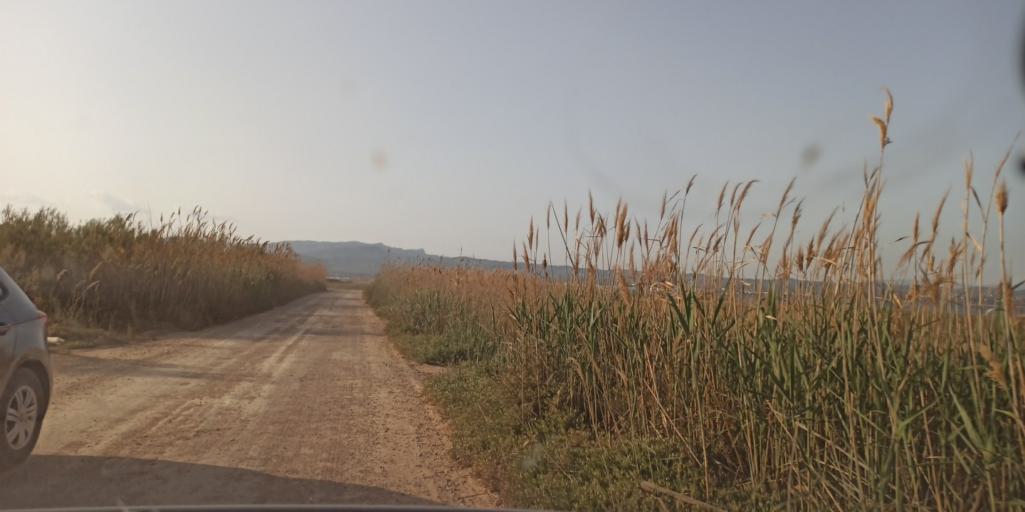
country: ES
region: Catalonia
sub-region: Provincia de Tarragona
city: L'Ampolla
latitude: 40.7764
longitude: 0.7233
